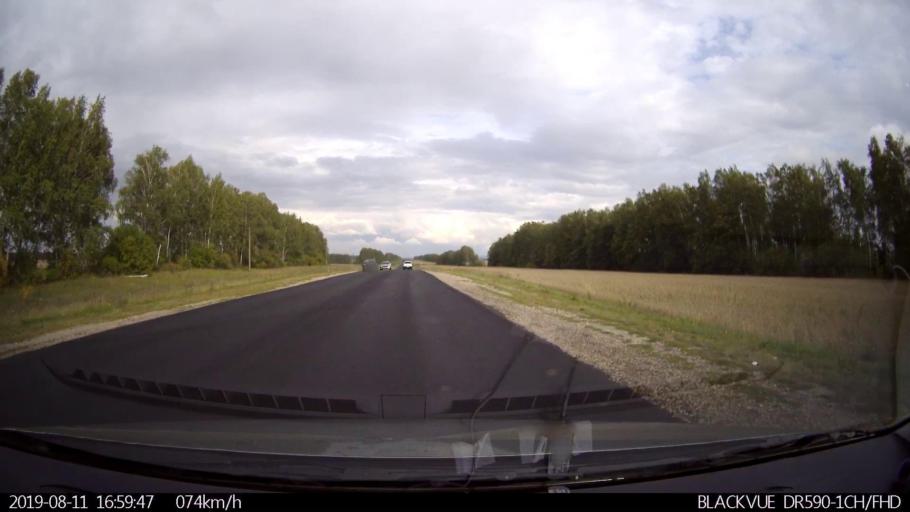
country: RU
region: Ulyanovsk
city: Mayna
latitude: 54.3113
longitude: 47.6654
